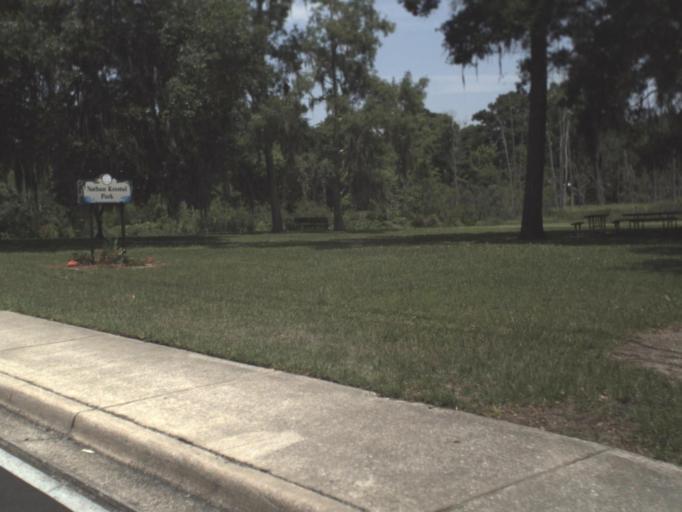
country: US
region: Florida
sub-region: Duval County
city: Jacksonville
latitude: 30.2529
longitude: -81.6399
